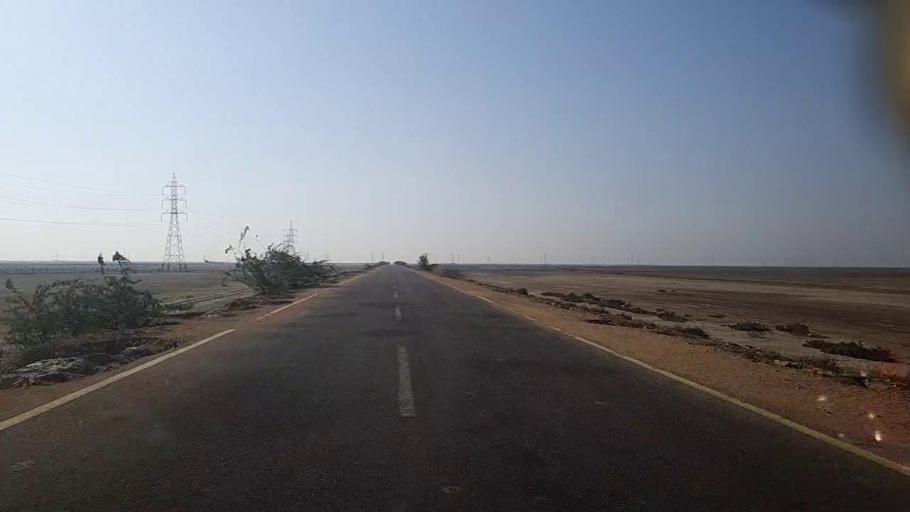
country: PK
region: Sindh
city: Mirpur Sakro
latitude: 24.6042
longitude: 67.4976
